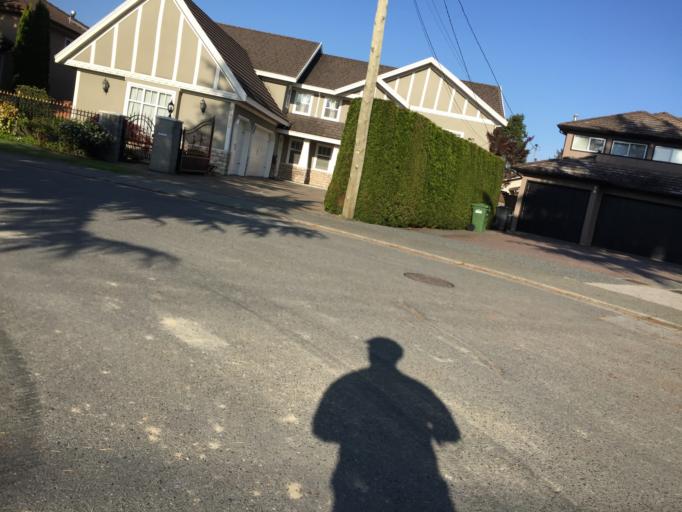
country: CA
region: British Columbia
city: Richmond
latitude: 49.1509
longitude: -123.1398
